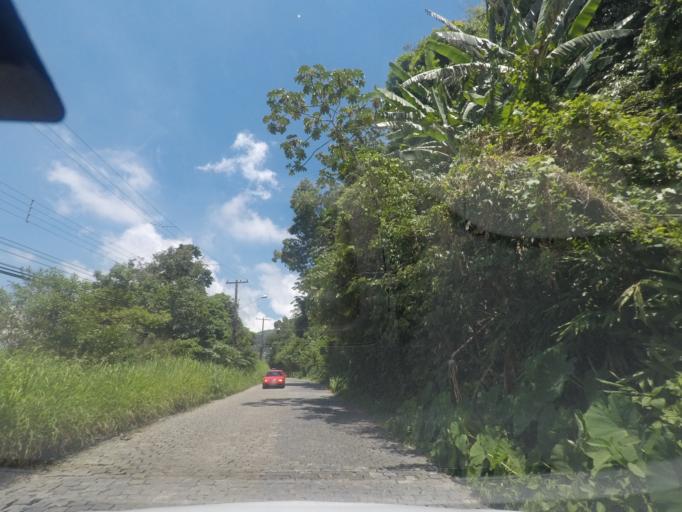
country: BR
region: Rio de Janeiro
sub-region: Petropolis
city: Petropolis
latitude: -22.5346
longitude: -43.1705
